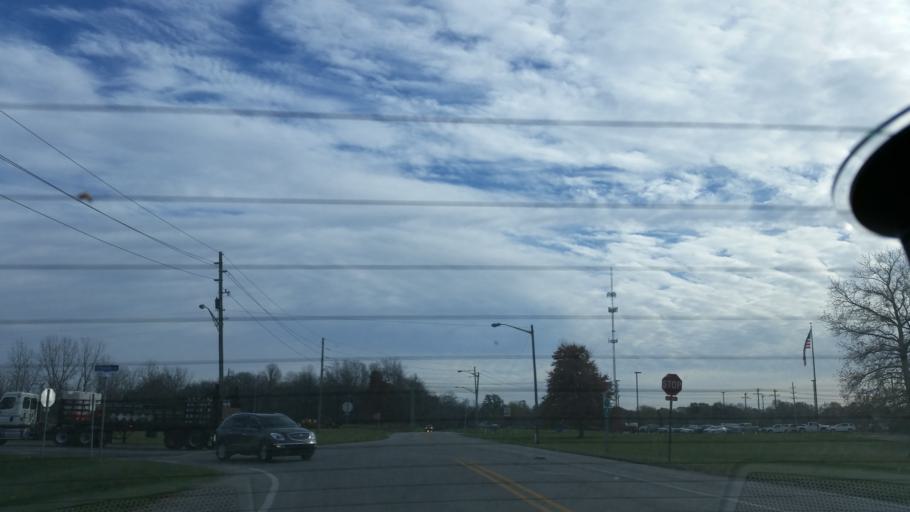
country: US
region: Indiana
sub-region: Howard County
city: Kokomo
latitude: 40.4691
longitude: -86.1521
